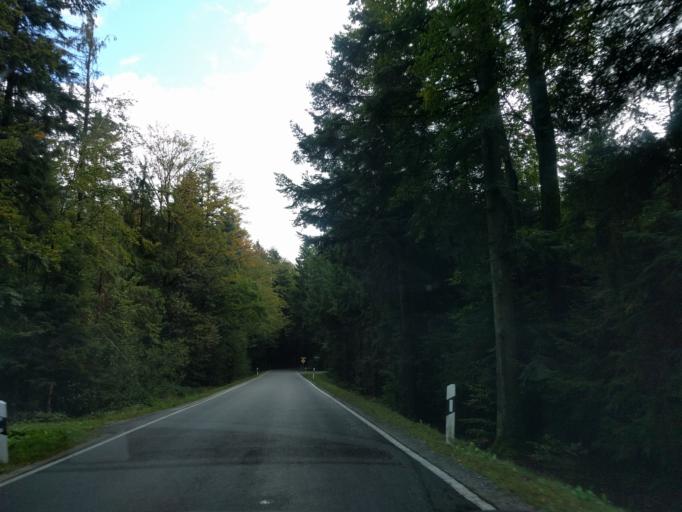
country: DE
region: Bavaria
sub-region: Lower Bavaria
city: Schaufling
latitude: 48.8328
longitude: 13.0536
